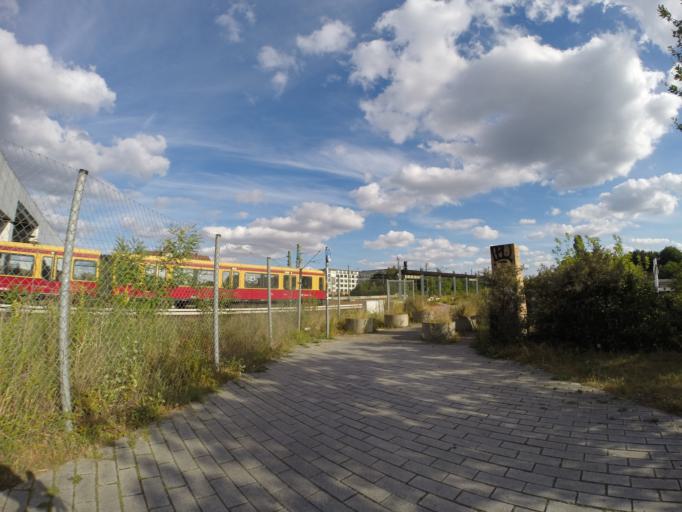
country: DE
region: Berlin
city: Schoneberg Bezirk
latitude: 52.4744
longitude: 13.3640
